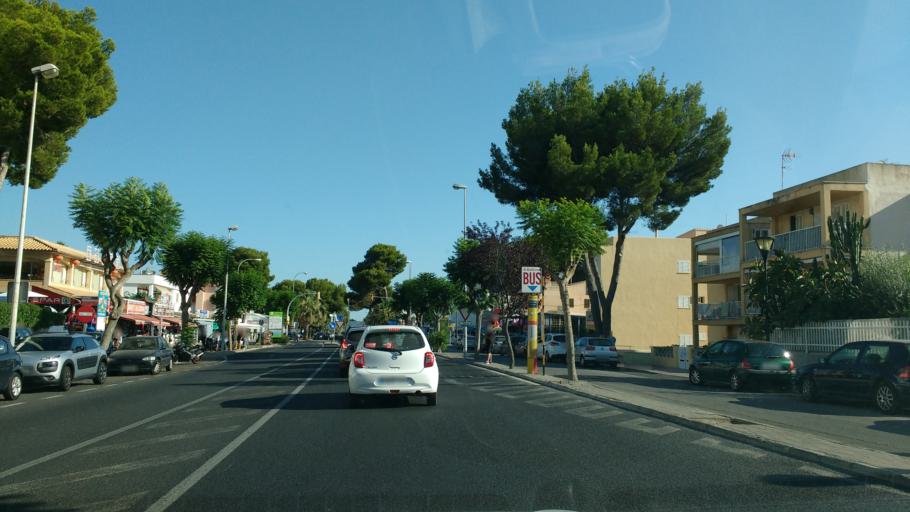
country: ES
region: Balearic Islands
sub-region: Illes Balears
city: Port d'Alcudia
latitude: 39.8162
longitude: 3.1139
